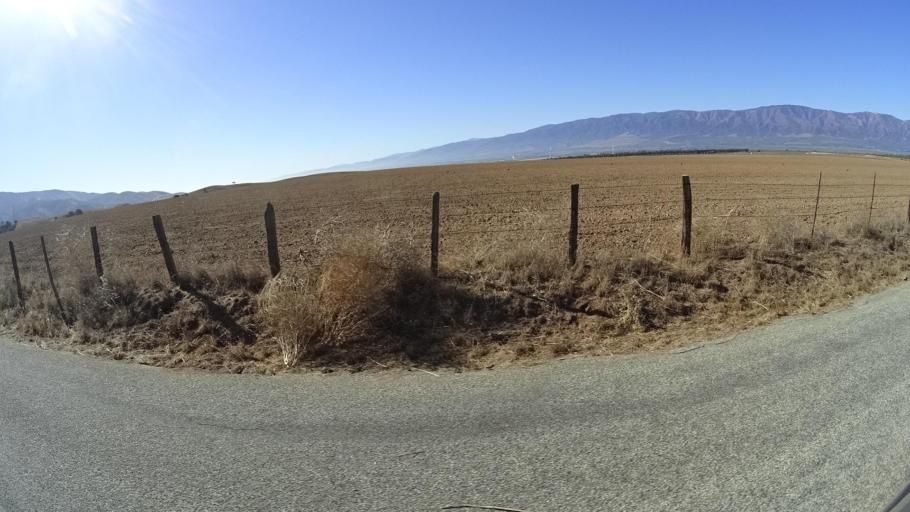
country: US
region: California
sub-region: Monterey County
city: Gonzales
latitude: 36.5112
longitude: -121.3601
